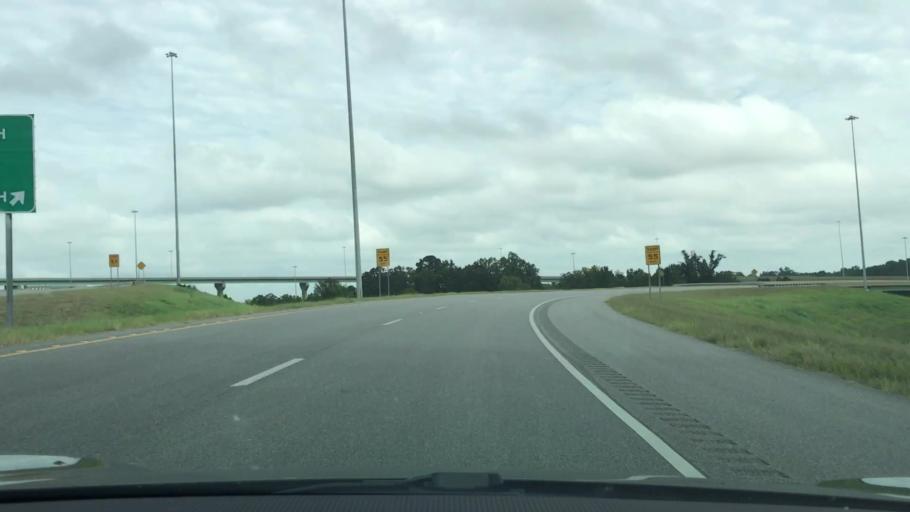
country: US
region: Alabama
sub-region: Montgomery County
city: Pike Road
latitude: 32.3644
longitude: -86.0777
